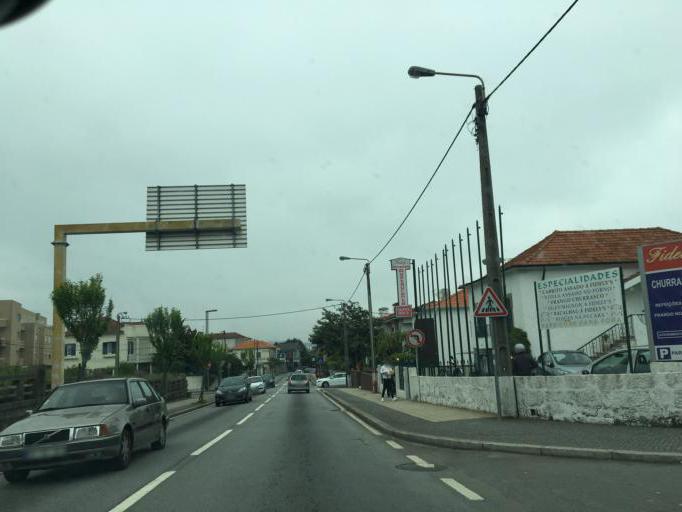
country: PT
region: Porto
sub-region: Maia
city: Anta
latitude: 41.2607
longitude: -8.6161
